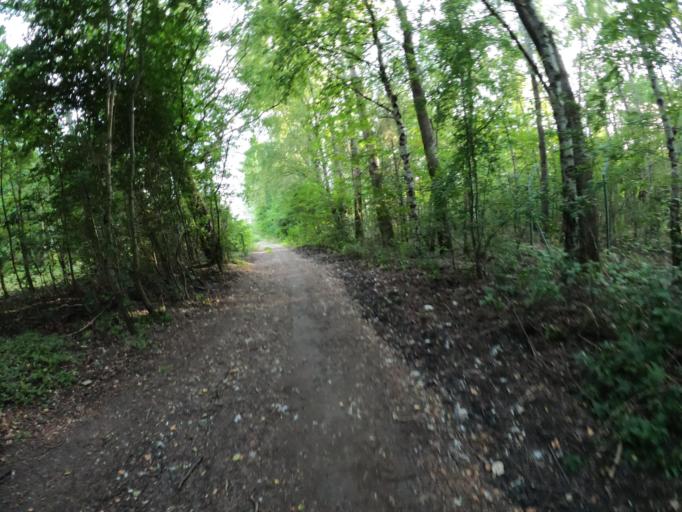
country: PL
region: West Pomeranian Voivodeship
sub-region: Koszalin
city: Koszalin
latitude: 54.1733
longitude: 16.2262
